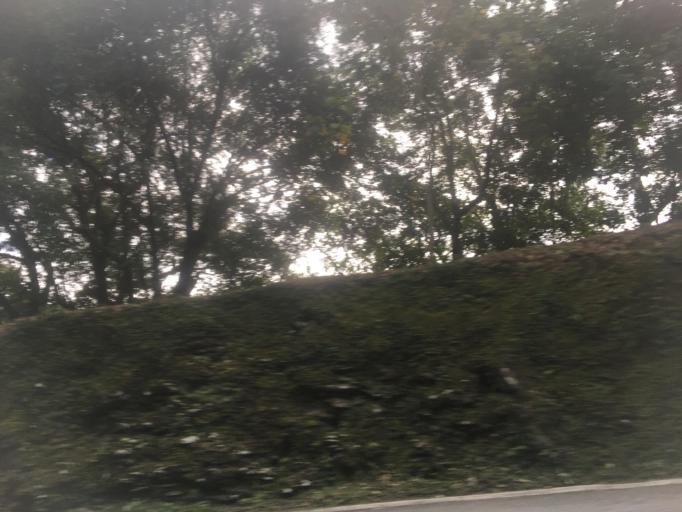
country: TW
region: Taiwan
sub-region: Yilan
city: Yilan
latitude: 24.6502
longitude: 121.5767
